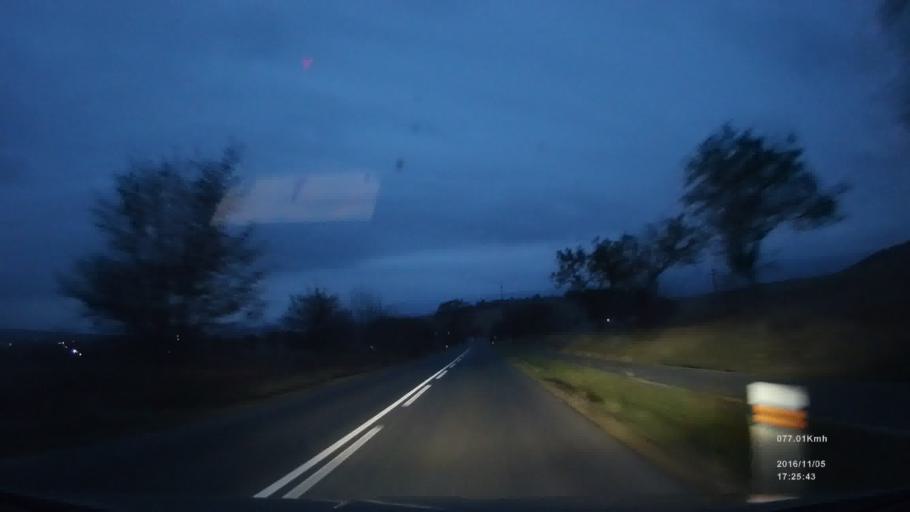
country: SK
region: Presovsky
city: Lubica
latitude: 49.0185
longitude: 20.4412
